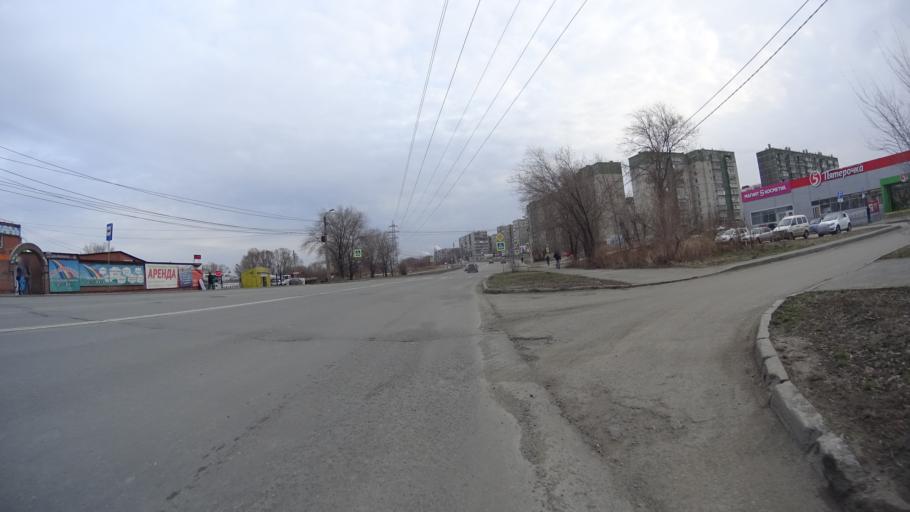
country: RU
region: Chelyabinsk
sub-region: Gorod Chelyabinsk
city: Chelyabinsk
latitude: 55.1875
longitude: 61.4843
